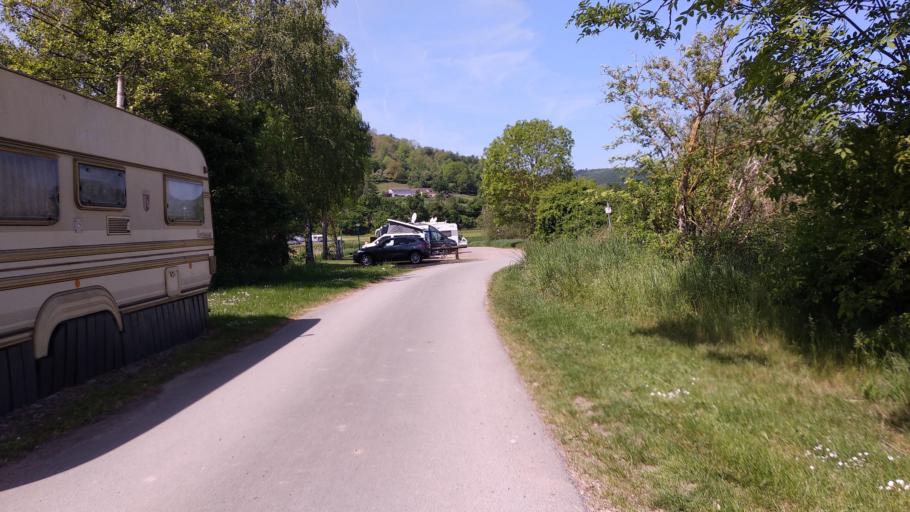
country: DE
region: North Rhine-Westphalia
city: Beverungen
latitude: 51.6511
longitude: 9.3774
